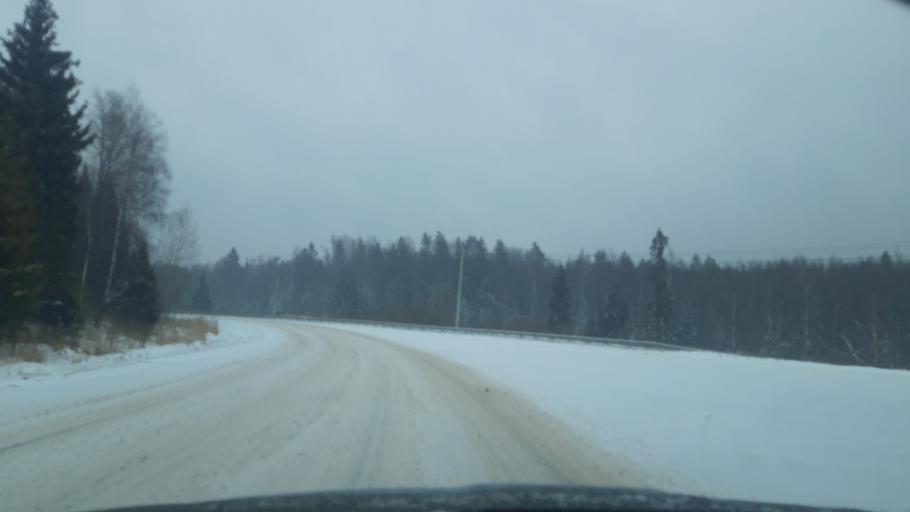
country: RU
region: Moskovskaya
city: Avtopoligon
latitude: 56.2617
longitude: 37.2691
